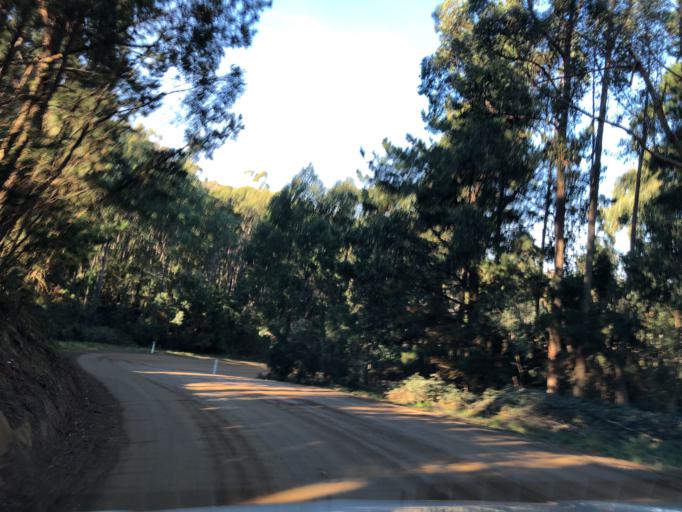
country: AU
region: Tasmania
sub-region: Kingborough
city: Kettering
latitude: -43.3501
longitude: 147.2356
